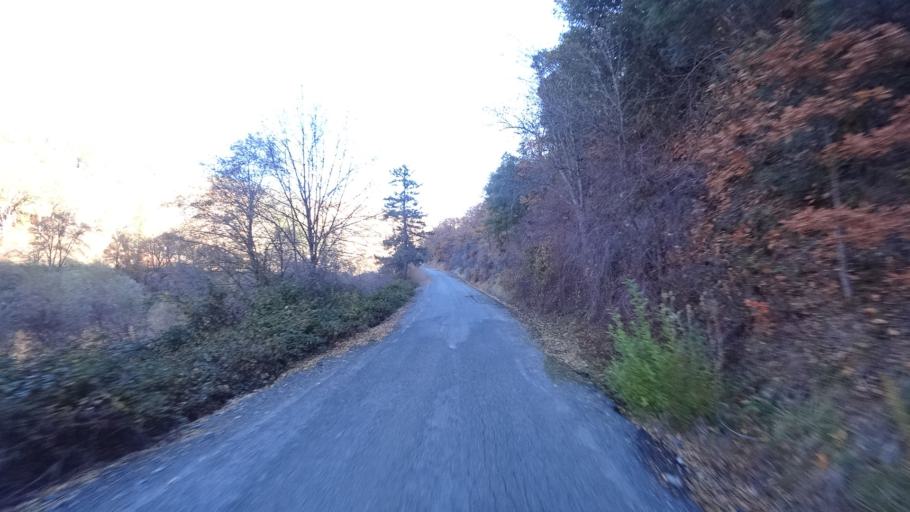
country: US
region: California
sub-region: Siskiyou County
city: Yreka
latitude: 41.8438
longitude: -122.9086
